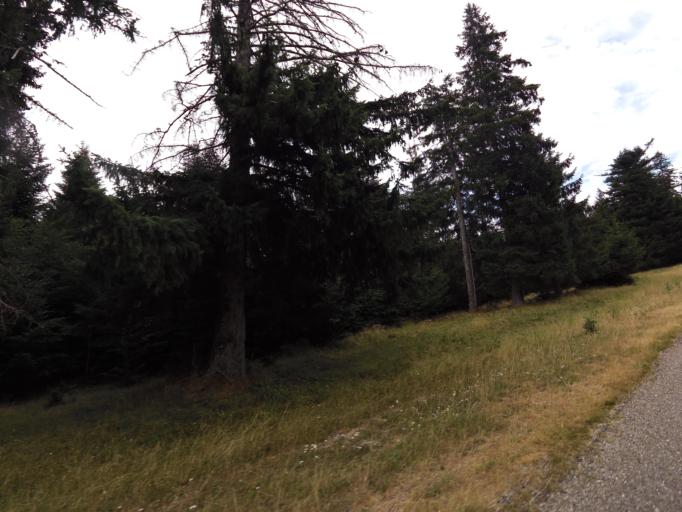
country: FR
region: Languedoc-Roussillon
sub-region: Departement du Gard
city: Valleraugue
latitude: 44.0788
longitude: 3.5752
